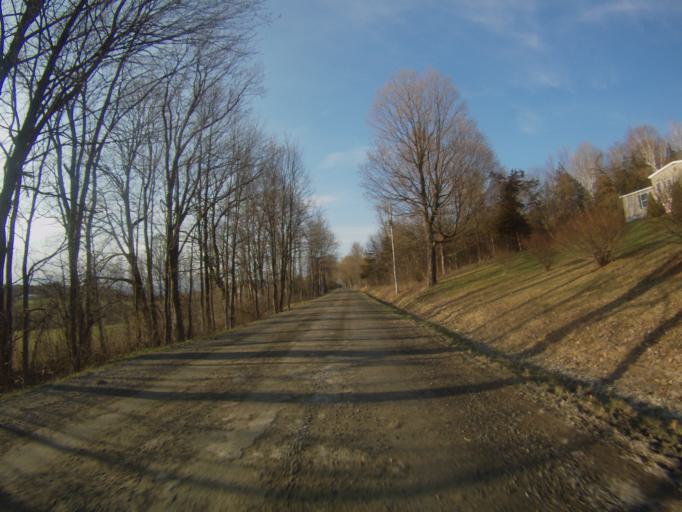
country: US
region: Vermont
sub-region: Addison County
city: Vergennes
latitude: 44.0560
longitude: -73.2923
